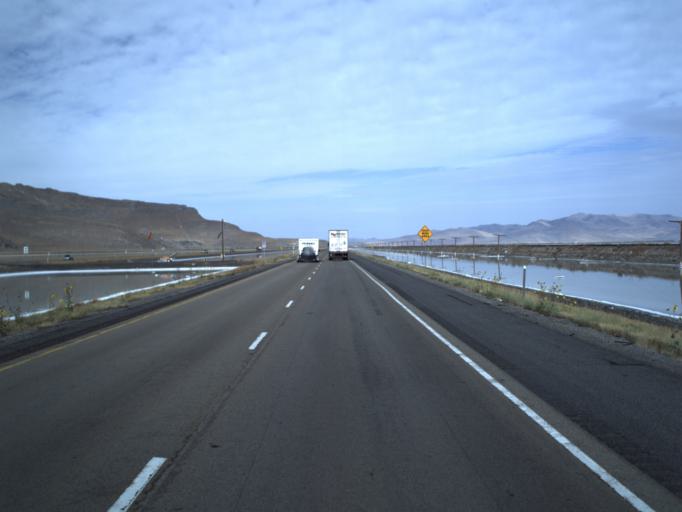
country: US
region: Utah
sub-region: Tooele County
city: Grantsville
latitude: 40.7302
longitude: -112.5877
